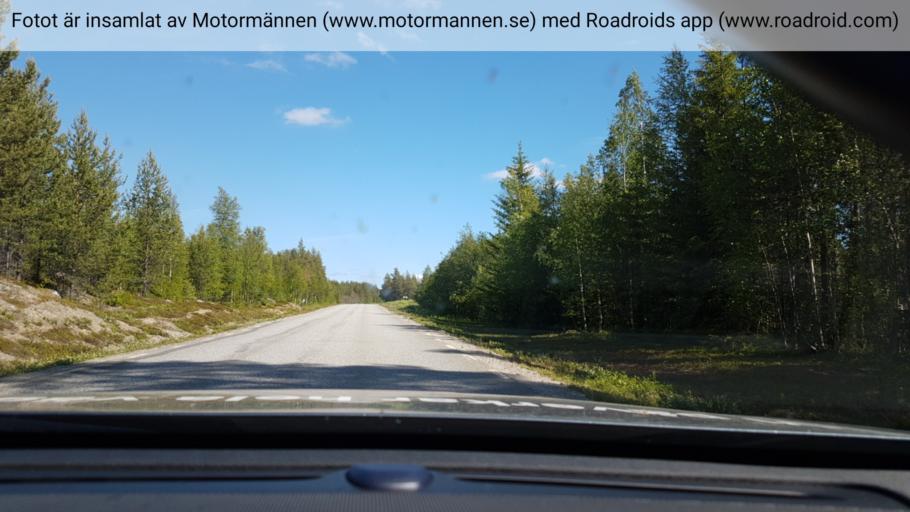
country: SE
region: Vaesterbotten
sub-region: Lycksele Kommun
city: Soderfors
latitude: 64.6339
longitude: 18.0139
